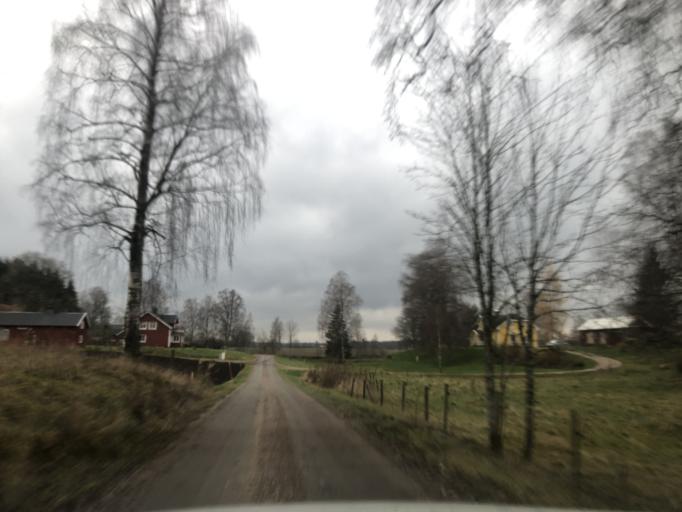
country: SE
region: Vaestra Goetaland
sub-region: Ulricehamns Kommun
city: Ulricehamn
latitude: 57.9053
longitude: 13.4863
